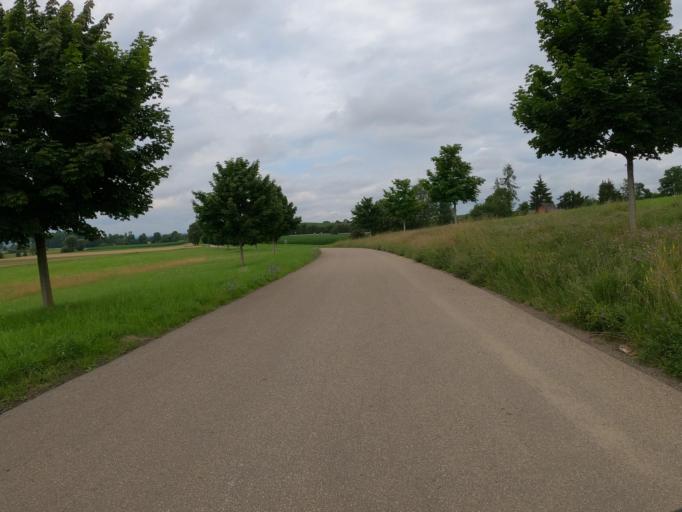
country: DE
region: Baden-Wuerttemberg
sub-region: Tuebingen Region
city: Rammingen
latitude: 48.5032
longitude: 10.1696
